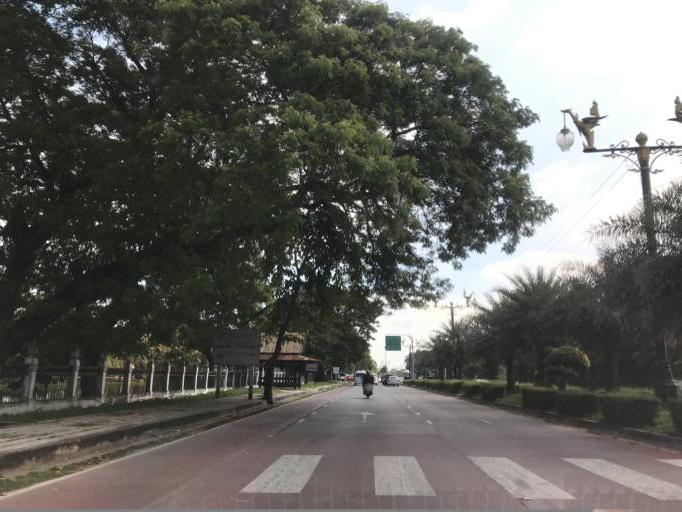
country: TH
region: Phra Nakhon Si Ayutthaya
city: Phra Nakhon Si Ayutthaya
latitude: 14.3512
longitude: 100.5608
